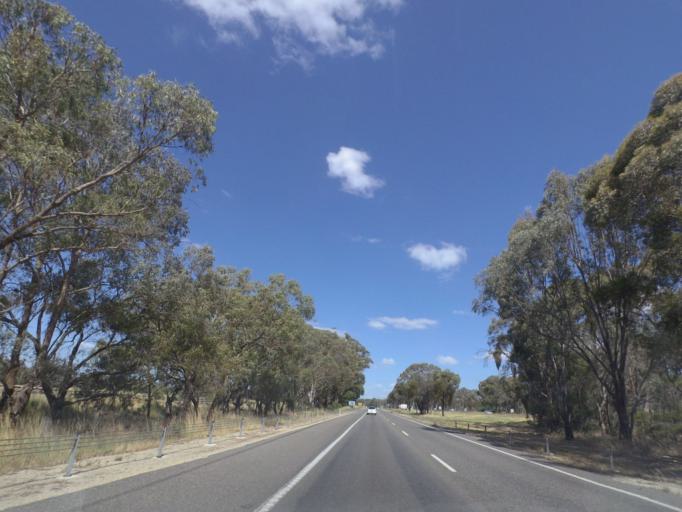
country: AU
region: Victoria
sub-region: Wodonga
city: Wodonga
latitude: -36.1002
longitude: 146.8217
